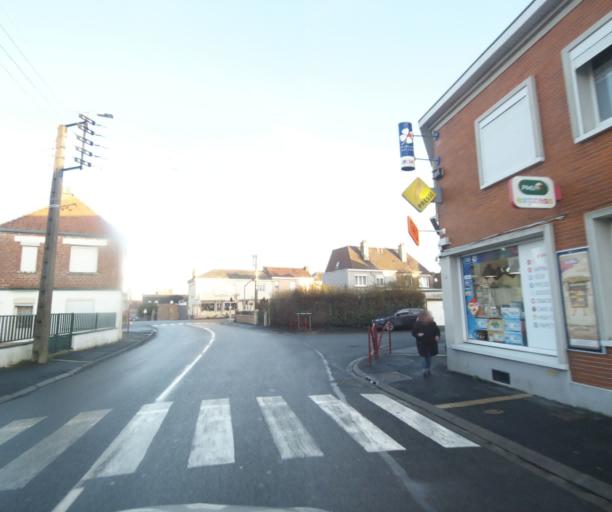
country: FR
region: Nord-Pas-de-Calais
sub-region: Departement du Nord
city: Quarouble
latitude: 50.3910
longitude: 3.6204
